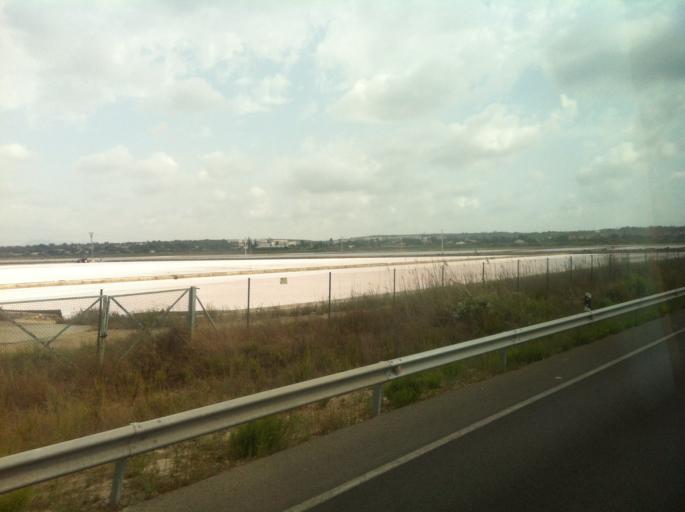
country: ES
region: Valencia
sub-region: Provincia de Alicante
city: Santa Pola
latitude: 38.1950
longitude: -0.5846
